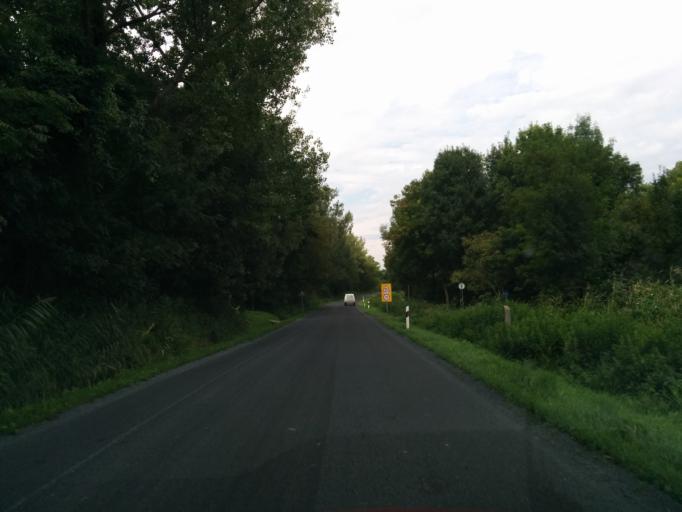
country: HU
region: Gyor-Moson-Sopron
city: Nagycenk
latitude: 47.6282
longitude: 16.7379
